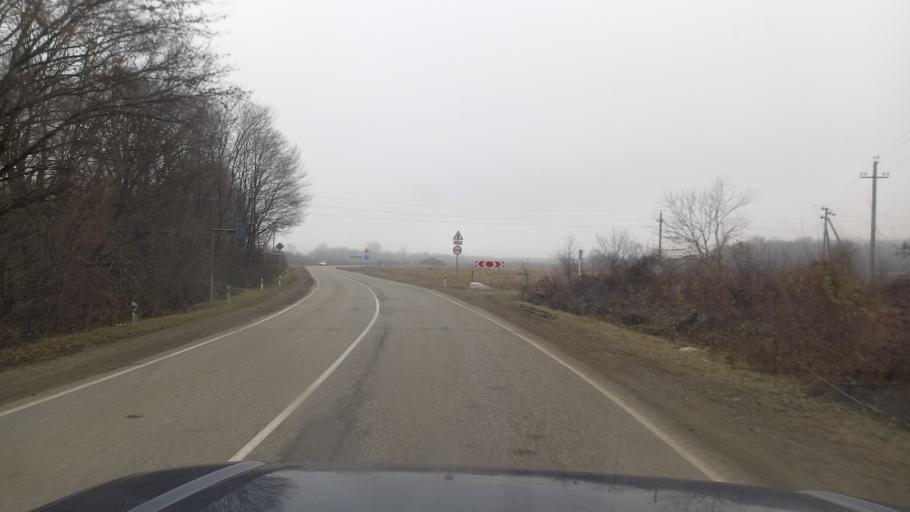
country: RU
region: Krasnodarskiy
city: Neftegorsk
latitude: 44.2903
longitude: 39.8232
